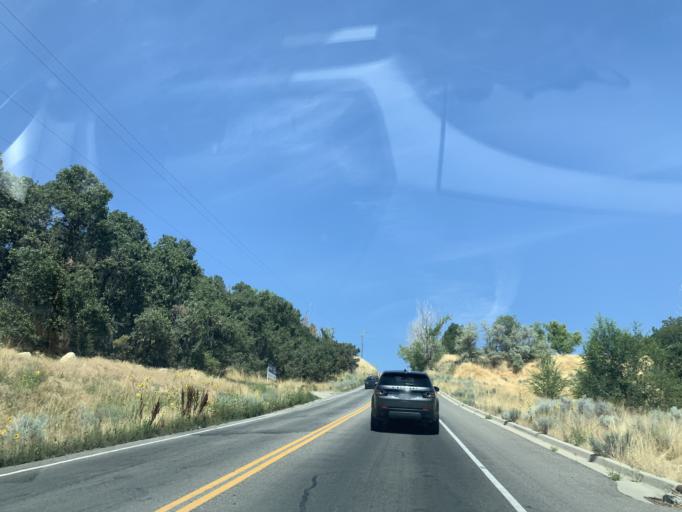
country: US
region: Utah
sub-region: Utah County
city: Lehi
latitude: 40.4232
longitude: -111.8305
